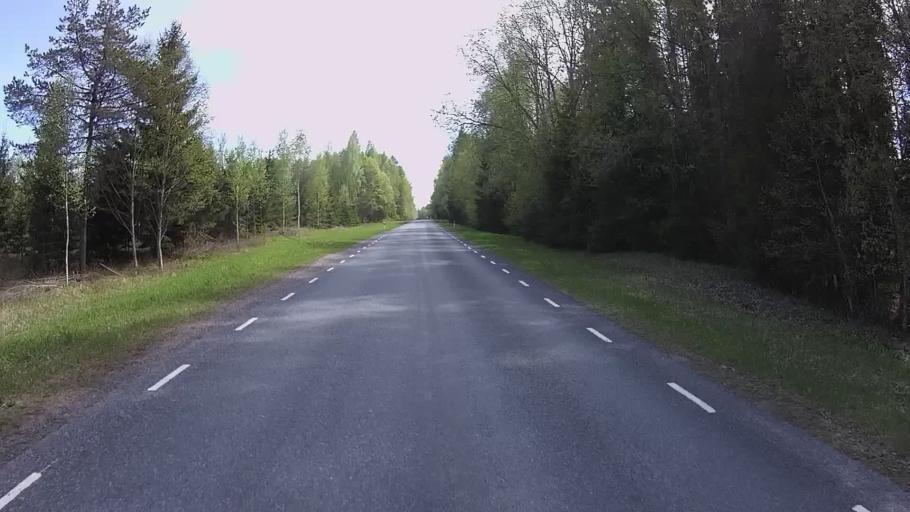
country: EE
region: Valgamaa
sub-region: Valga linn
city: Valga
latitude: 57.7042
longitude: 26.2409
